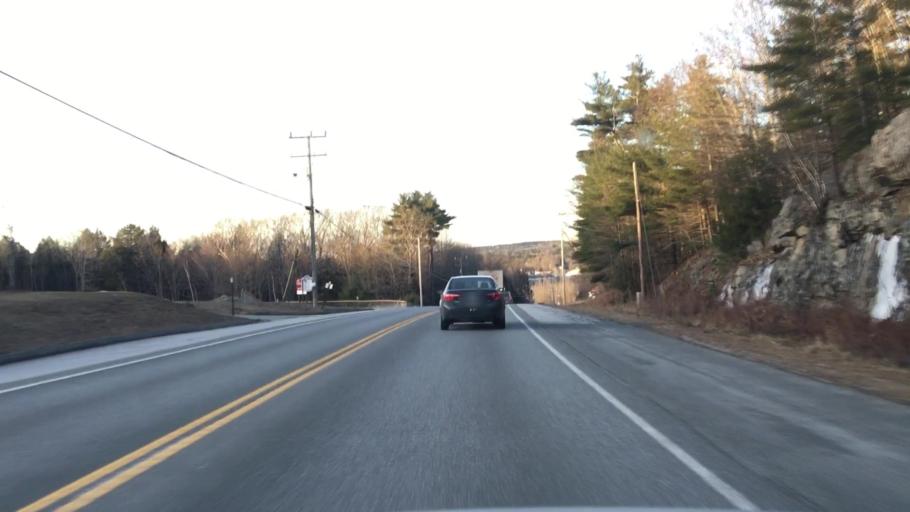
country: US
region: Maine
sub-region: Hancock County
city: Dedham
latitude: 44.7273
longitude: -68.6225
